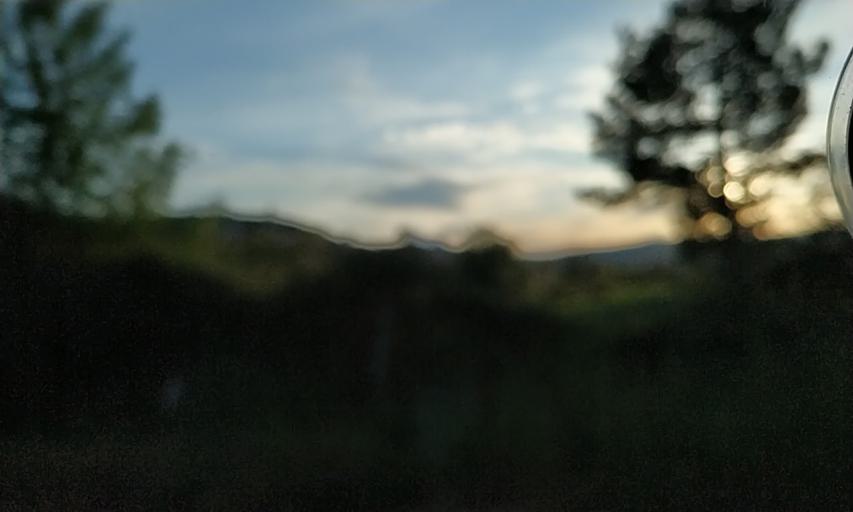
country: ES
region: Galicia
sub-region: Provincia de Ourense
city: Verin
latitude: 41.9237
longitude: -7.4431
